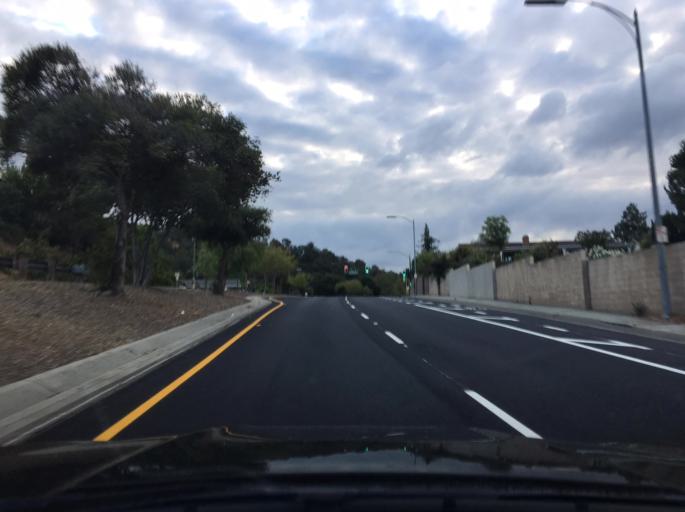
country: US
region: California
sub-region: Santa Clara County
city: Cambrian Park
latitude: 37.2214
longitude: -121.8918
